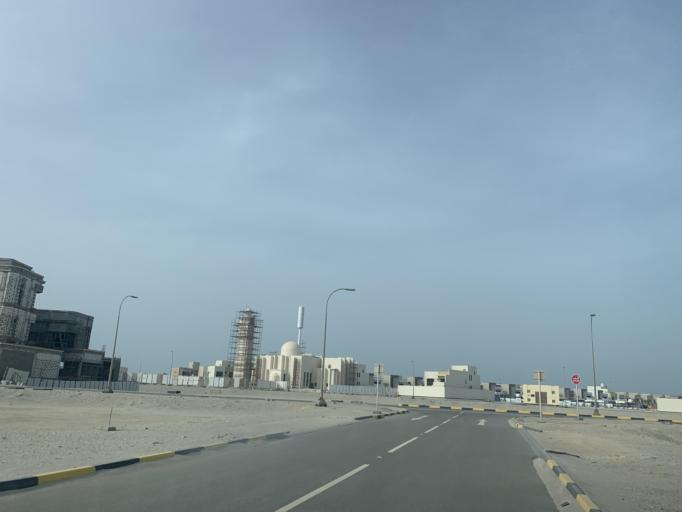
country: BH
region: Muharraq
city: Al Muharraq
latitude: 26.3210
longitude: 50.6247
